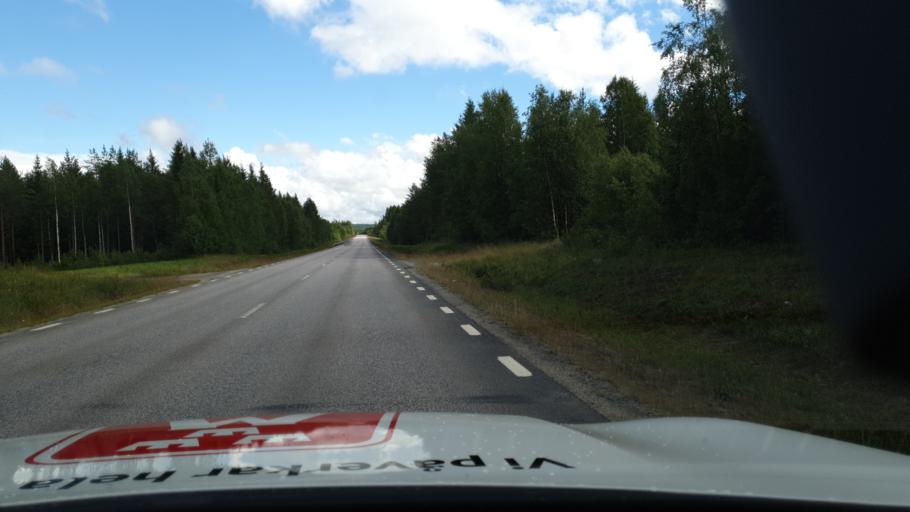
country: SE
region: Vaesterbotten
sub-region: Vannas Kommun
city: Vaennaes
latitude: 63.9112
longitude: 19.6612
